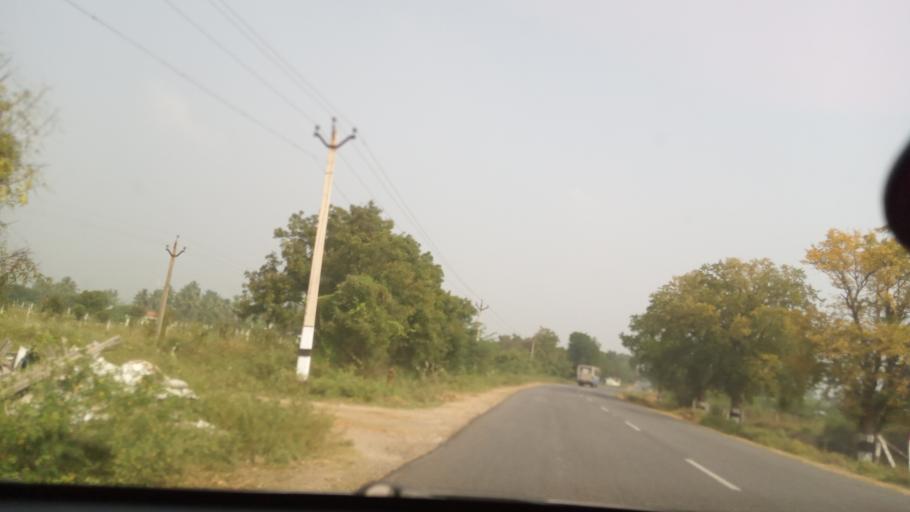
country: IN
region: Tamil Nadu
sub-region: Erode
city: Punjai Puliyampatti
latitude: 11.4108
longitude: 77.1929
